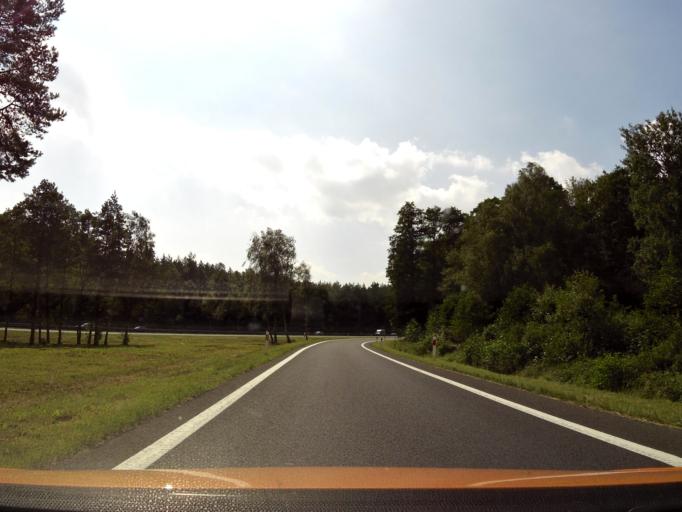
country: PL
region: West Pomeranian Voivodeship
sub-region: Powiat goleniowski
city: Goleniow
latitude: 53.5868
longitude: 14.8166
